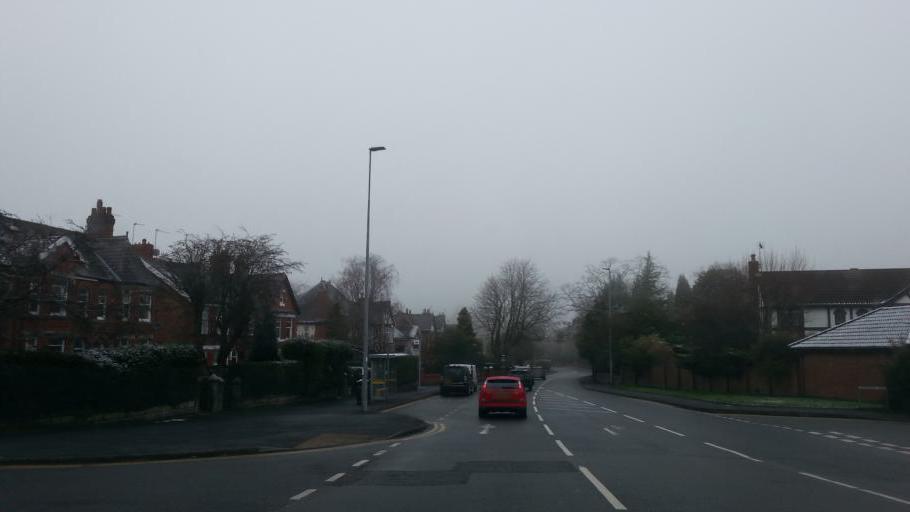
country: GB
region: England
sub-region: Cheshire East
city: Congleton
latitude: 53.1580
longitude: -2.1938
